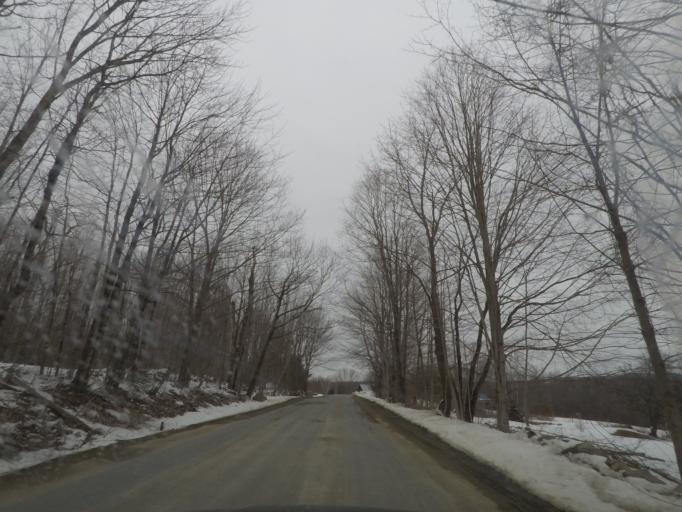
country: US
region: New York
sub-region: Rensselaer County
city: Averill Park
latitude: 42.5558
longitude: -73.4128
